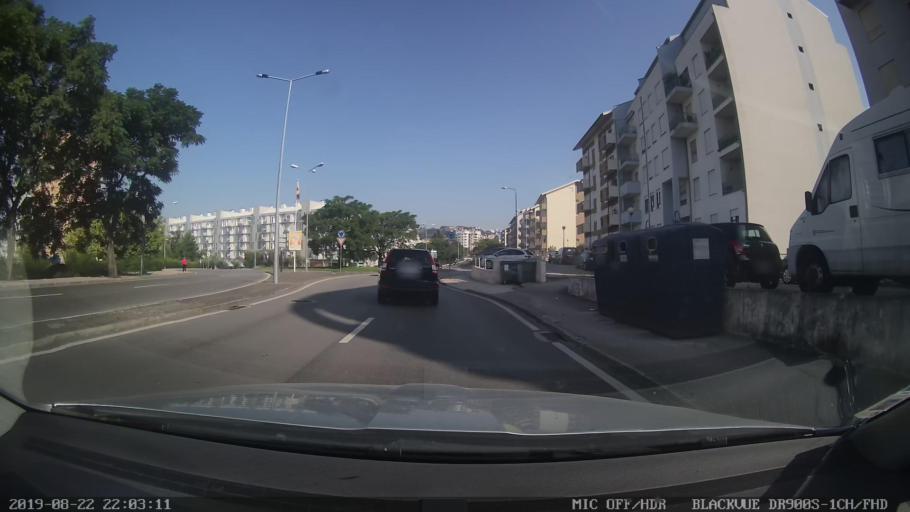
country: PT
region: Coimbra
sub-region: Coimbra
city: Coimbra
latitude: 40.2013
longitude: -8.3995
